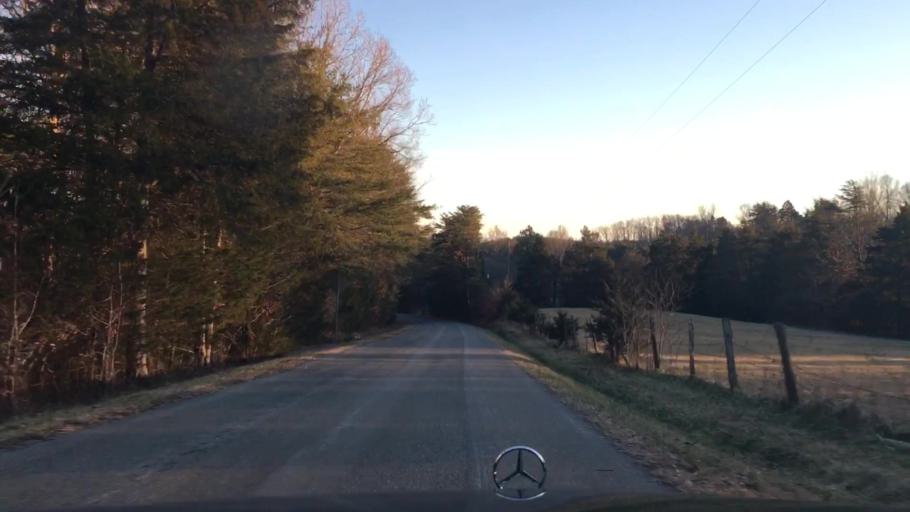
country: US
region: Virginia
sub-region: Campbell County
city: Altavista
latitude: 37.1826
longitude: -79.2953
